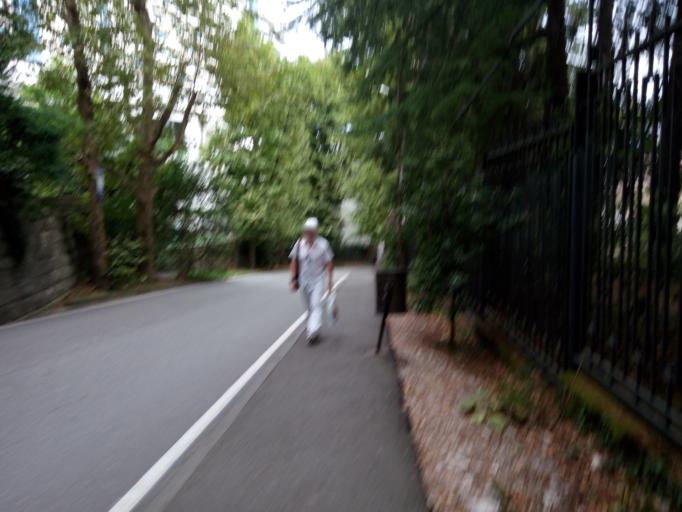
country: RU
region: Krasnodarskiy
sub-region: Sochi City
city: Sochi
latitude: 43.5633
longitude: 39.7612
